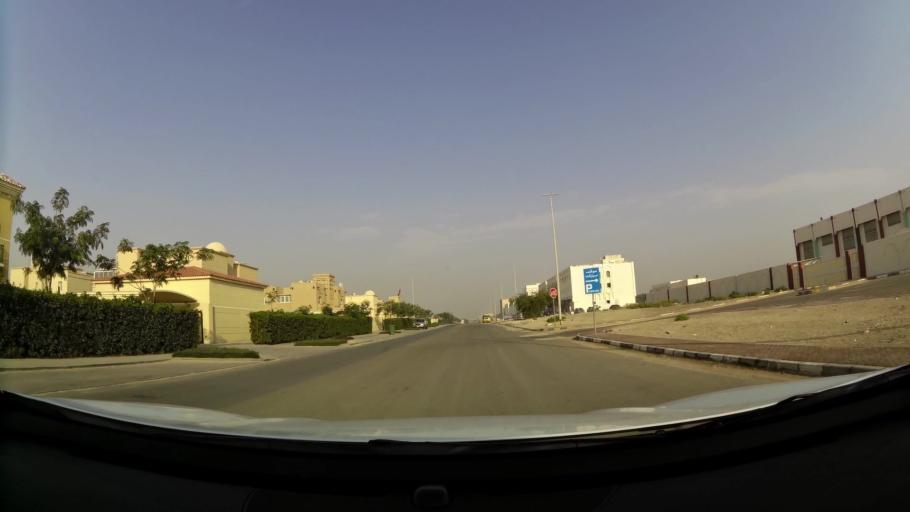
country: AE
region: Abu Dhabi
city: Abu Dhabi
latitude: 24.2993
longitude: 54.6199
